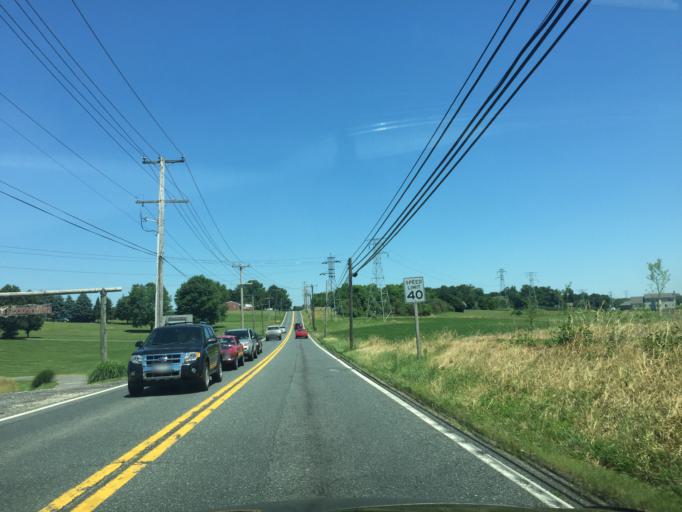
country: US
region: Maryland
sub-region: Harford County
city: Jarrettsville
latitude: 39.5878
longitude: -76.4730
